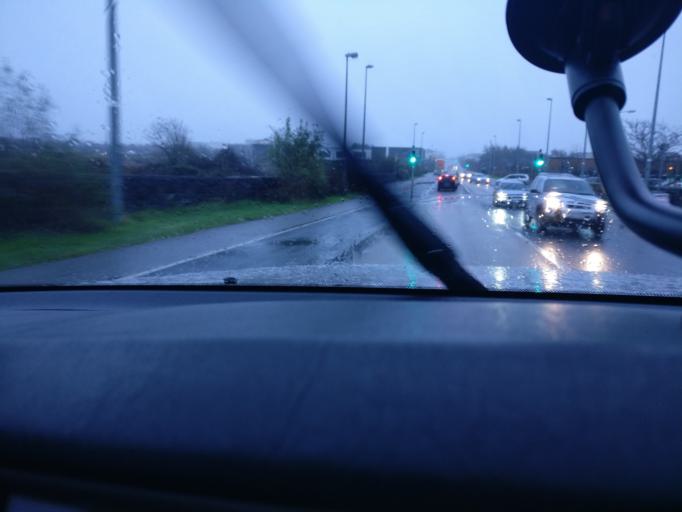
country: IE
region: Connaught
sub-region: County Galway
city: Claregalway
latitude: 53.2862
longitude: -8.9833
